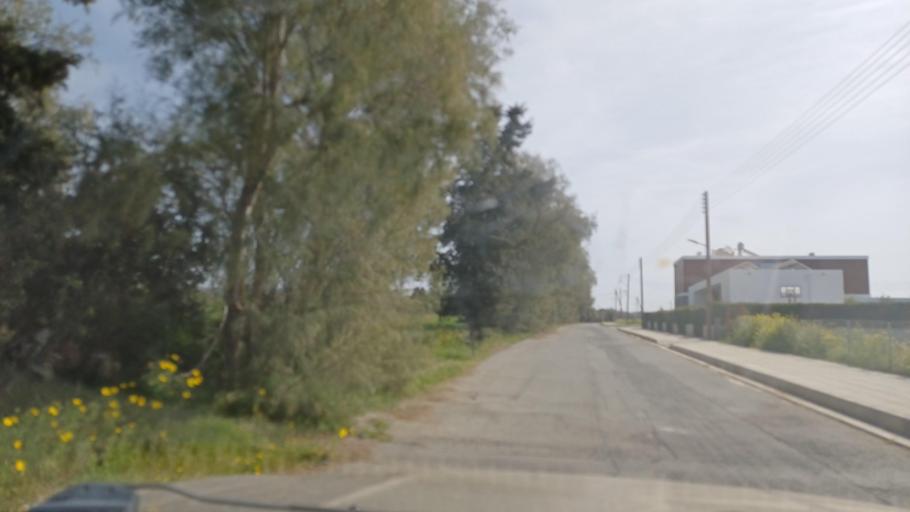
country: CY
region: Pafos
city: Paphos
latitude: 34.7537
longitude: 32.4703
